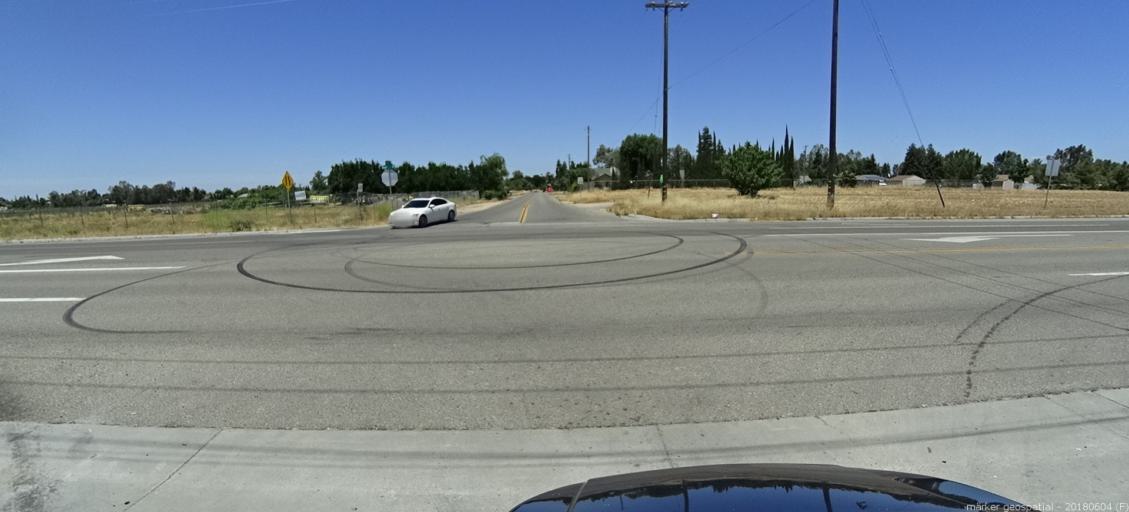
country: US
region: California
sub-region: Madera County
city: Madera Acres
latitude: 36.9963
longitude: -120.0915
